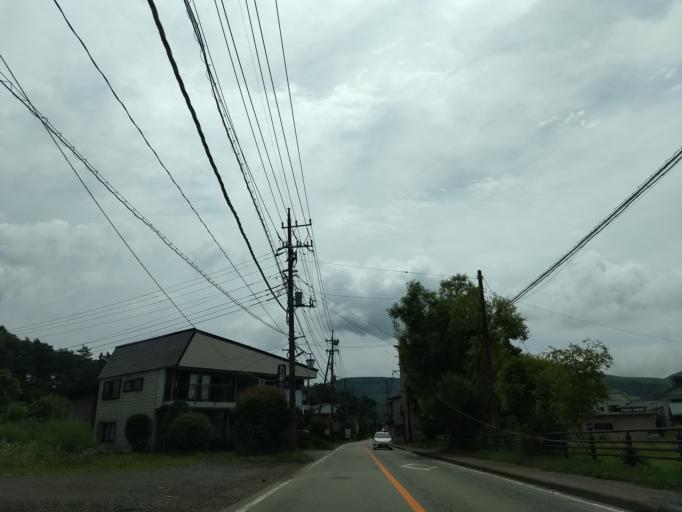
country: JP
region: Shizuoka
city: Gotemba
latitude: 35.4286
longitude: 138.8993
